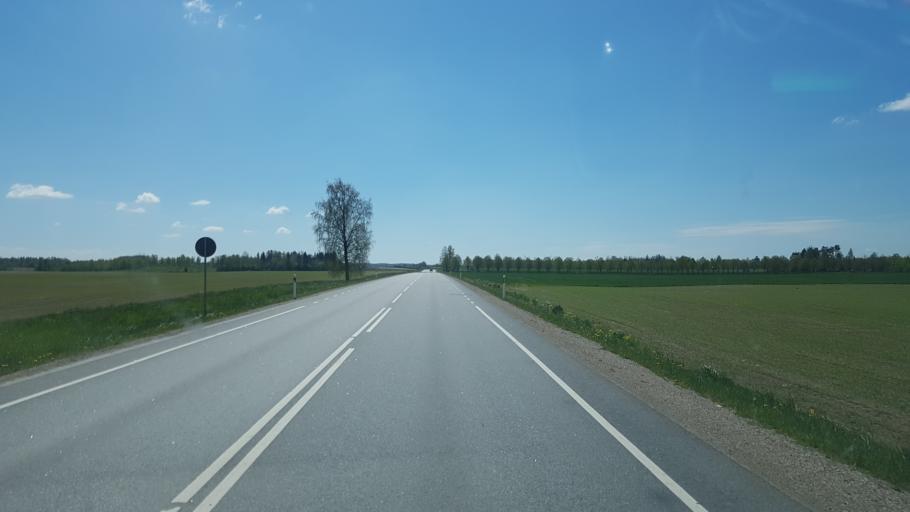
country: EE
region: Viljandimaa
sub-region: Viiratsi vald
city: Viiratsi
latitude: 58.3507
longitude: 25.6257
